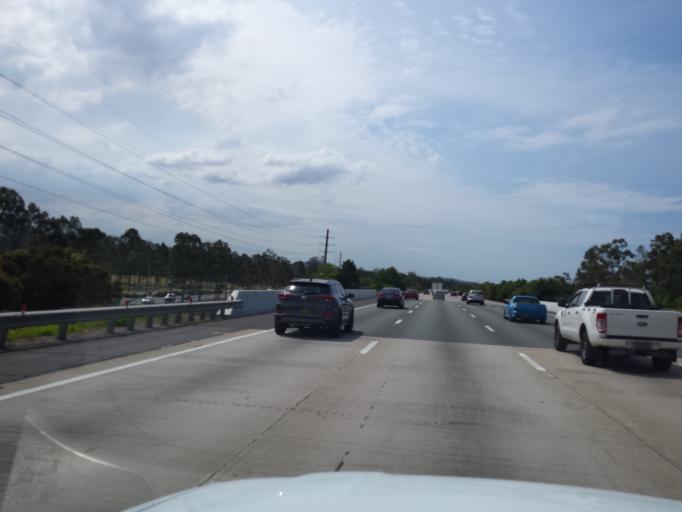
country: AU
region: Queensland
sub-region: Gold Coast
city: Oxenford
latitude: -27.9080
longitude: 153.3174
